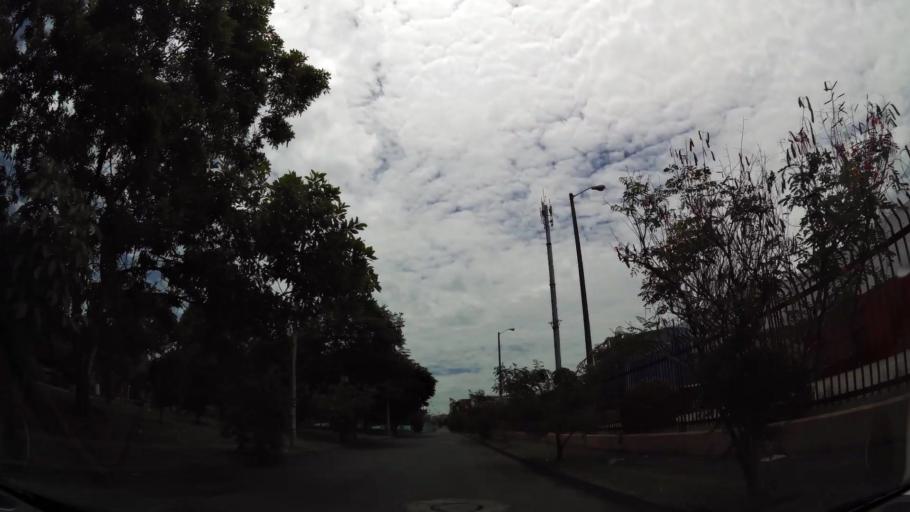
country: CO
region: Valle del Cauca
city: Cali
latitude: 3.3740
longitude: -76.5226
